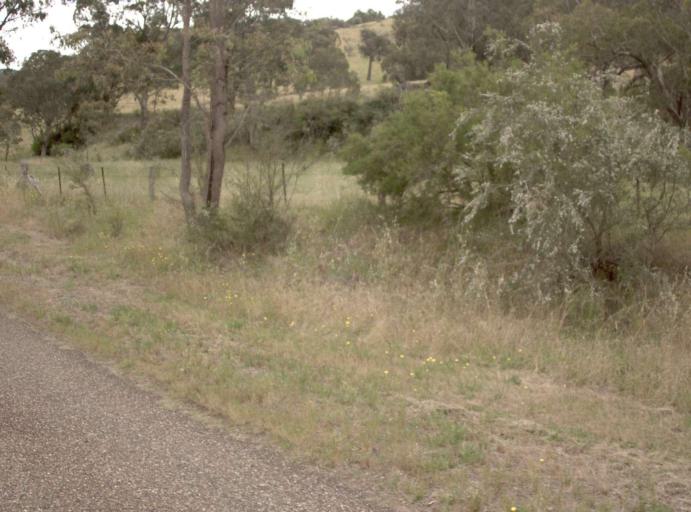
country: AU
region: Victoria
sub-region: East Gippsland
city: Bairnsdale
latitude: -37.5051
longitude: 147.1996
